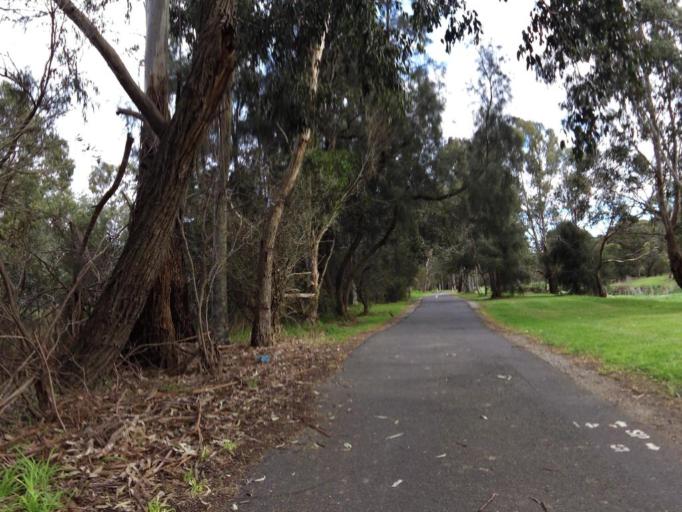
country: AU
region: Victoria
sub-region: Knox
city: Wantirna
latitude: -37.8407
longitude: 145.2139
